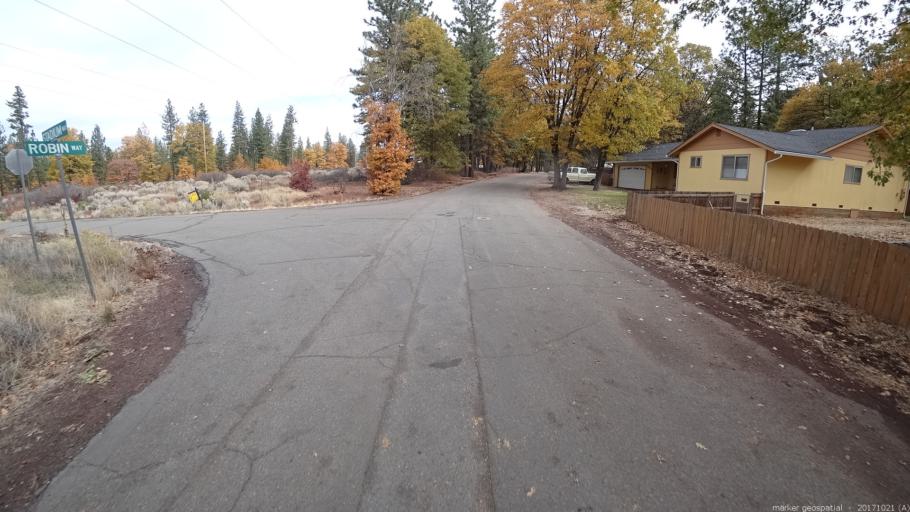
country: US
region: California
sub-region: Shasta County
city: Burney
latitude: 40.9223
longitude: -121.6262
